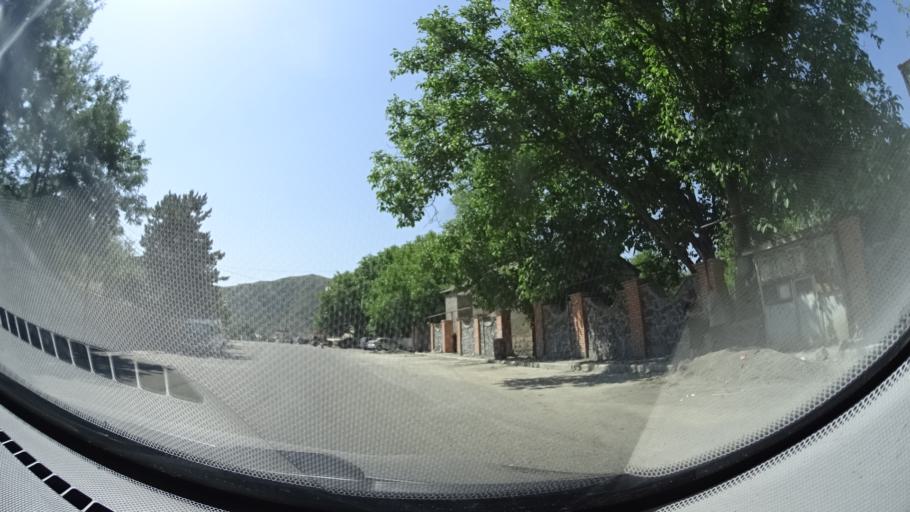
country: GE
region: Samtskhe-Javakheti
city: Aspindza
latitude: 41.5695
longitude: 43.2549
